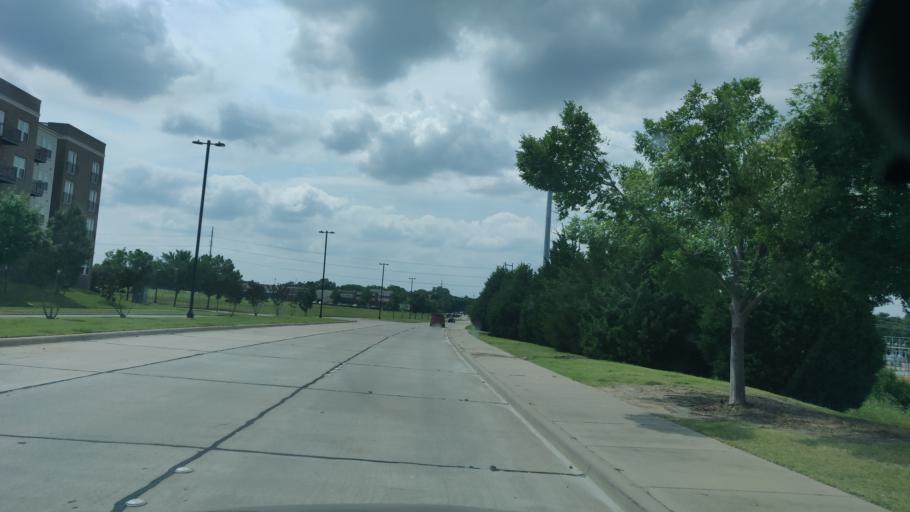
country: US
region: Texas
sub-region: Dallas County
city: Sachse
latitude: 32.9559
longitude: -96.6118
